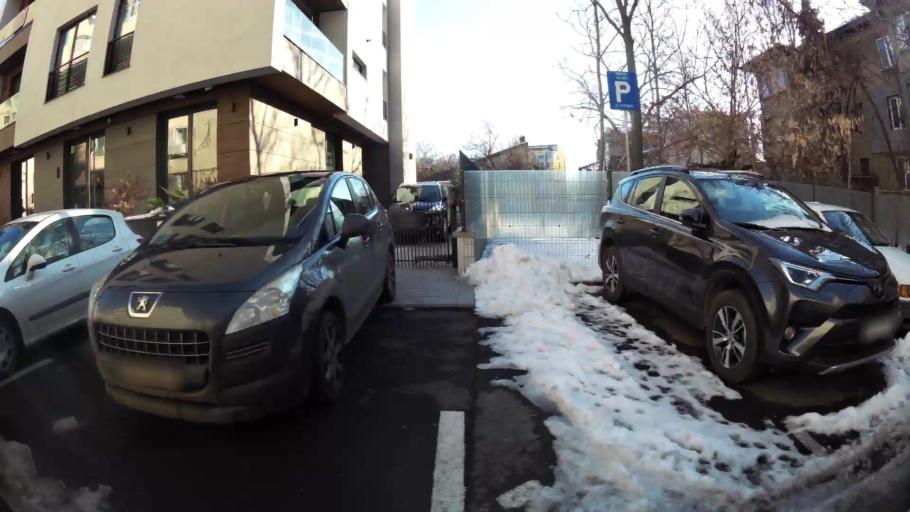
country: RO
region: Bucuresti
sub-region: Municipiul Bucuresti
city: Bucuresti
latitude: 44.4241
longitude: 26.0769
